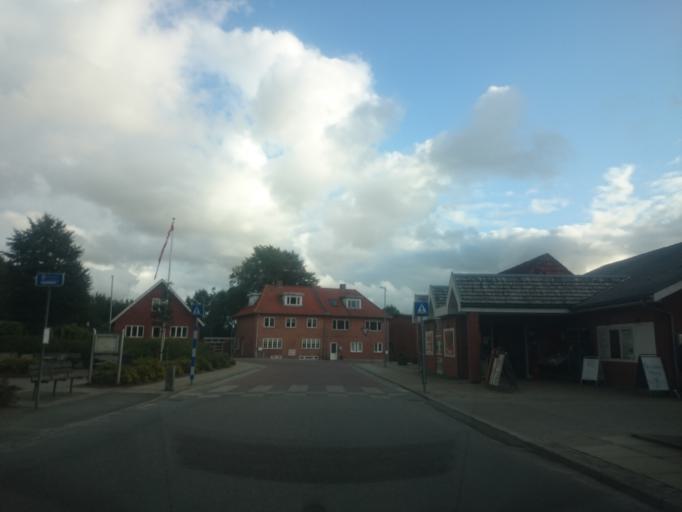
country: DK
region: South Denmark
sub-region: Billund Kommune
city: Grindsted
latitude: 55.6486
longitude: 8.8213
